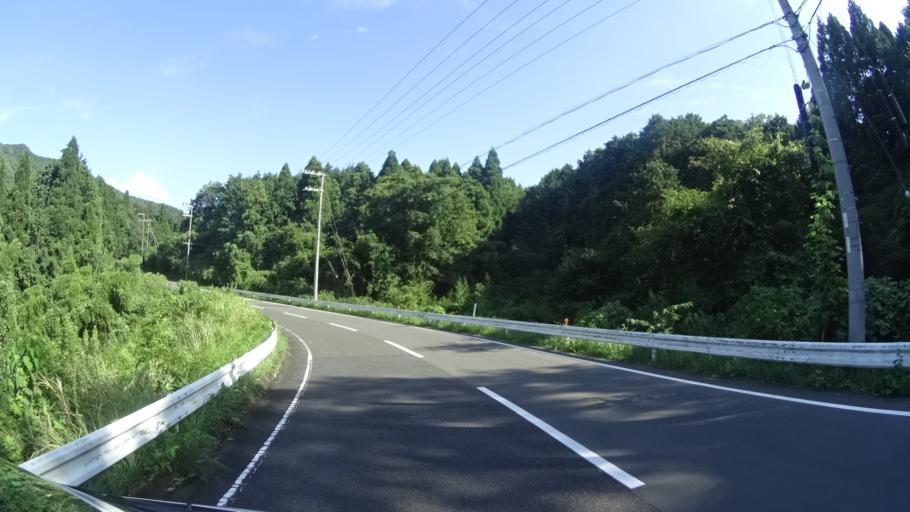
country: JP
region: Kyoto
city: Ayabe
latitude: 35.2865
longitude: 135.3304
